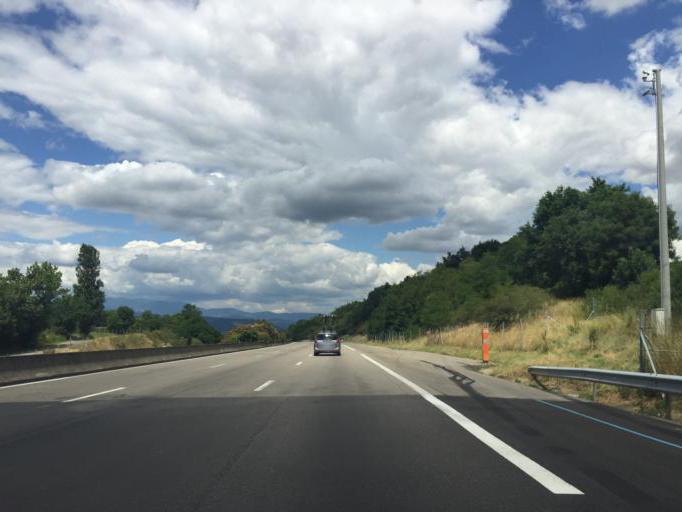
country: FR
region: Rhone-Alpes
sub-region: Departement de la Drome
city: Beausemblant
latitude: 45.2237
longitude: 4.8573
